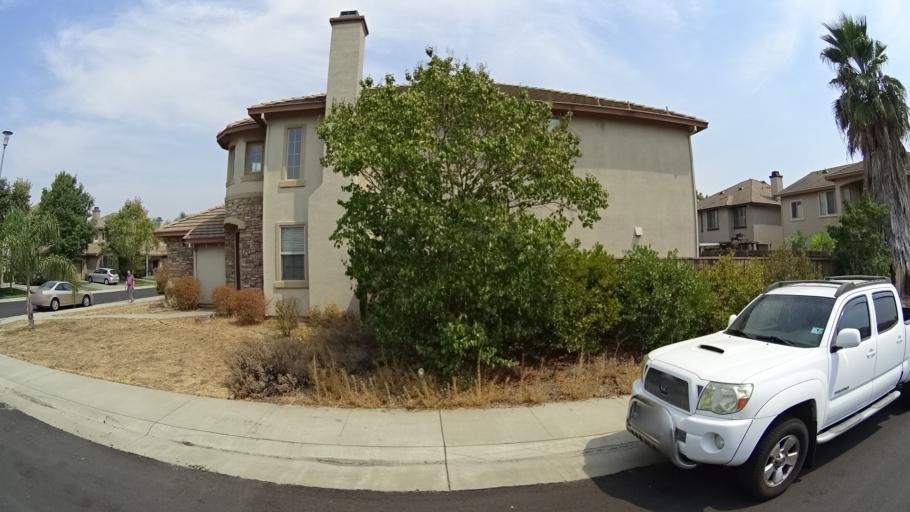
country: US
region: California
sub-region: Sacramento County
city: Laguna
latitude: 38.3823
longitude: -121.4287
